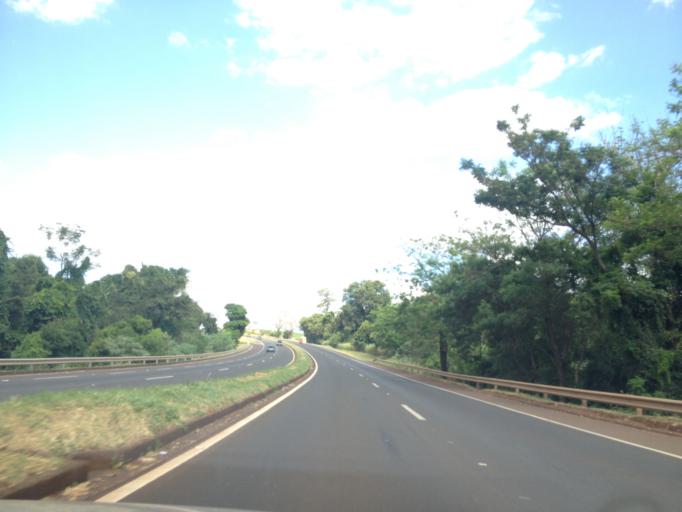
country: BR
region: Parana
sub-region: Marialva
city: Marialva
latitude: -23.4890
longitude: -51.8179
